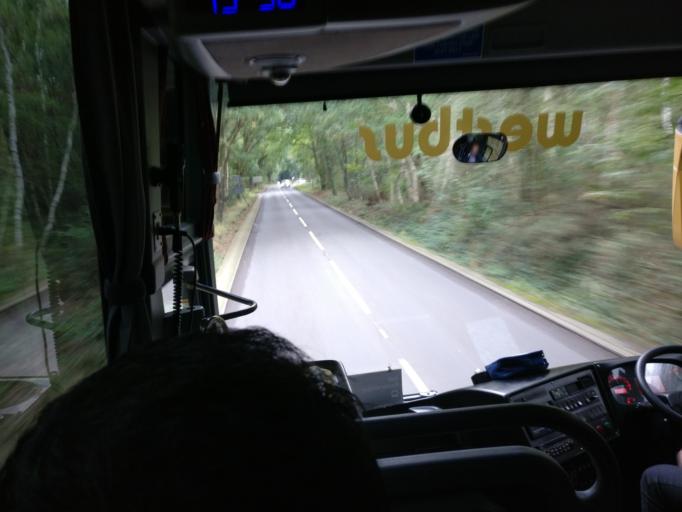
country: GB
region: England
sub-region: Surrey
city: Woking
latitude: 51.3330
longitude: -0.5728
